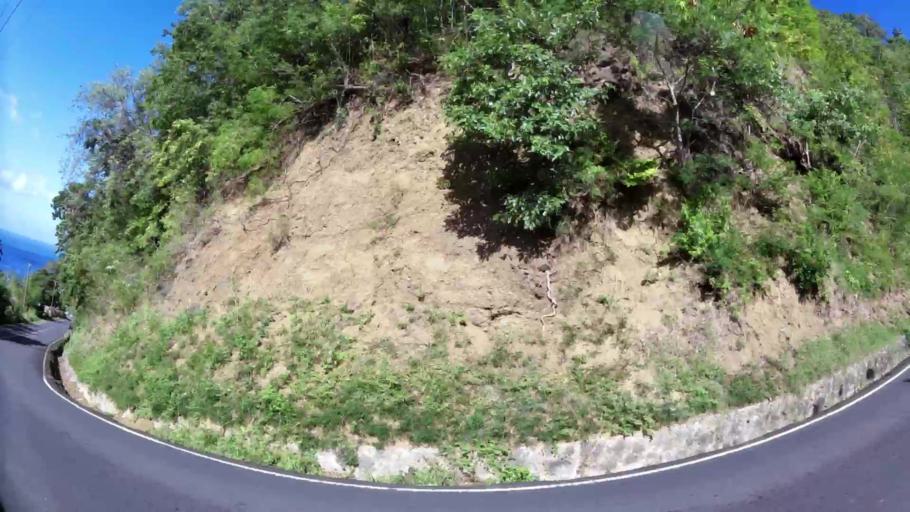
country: LC
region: Soufriere
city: Soufriere
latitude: 13.8607
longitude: -61.0540
